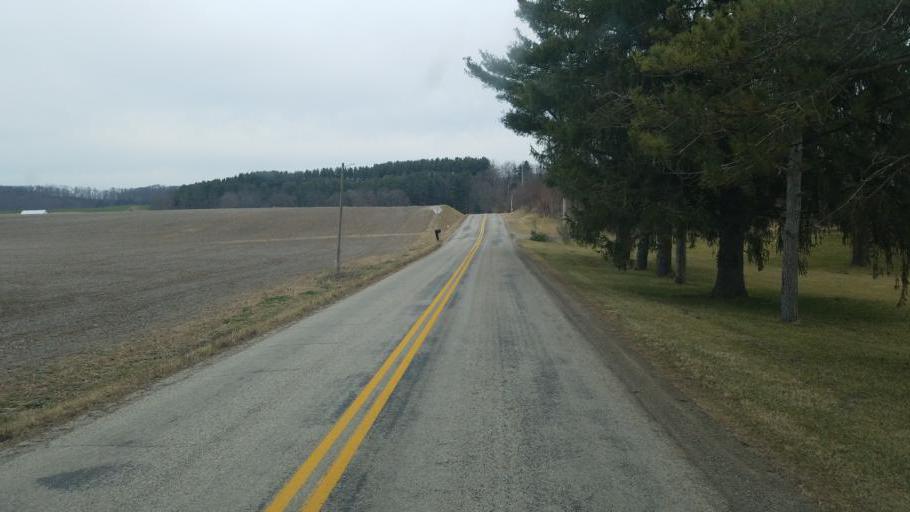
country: US
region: Ohio
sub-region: Ashland County
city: Loudonville
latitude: 40.6573
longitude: -82.2499
